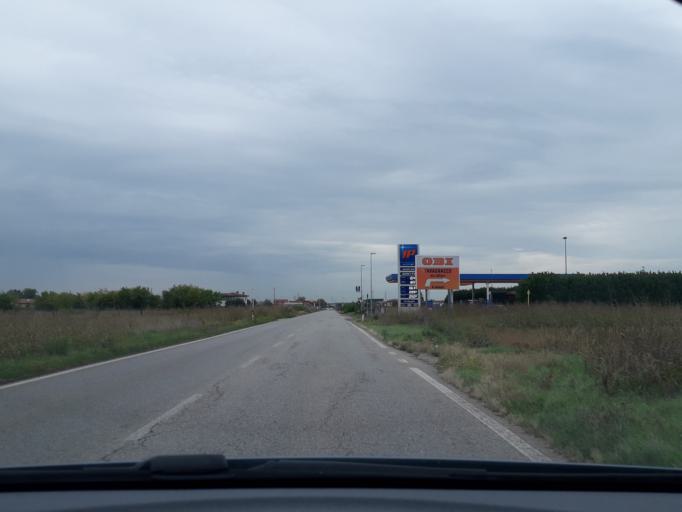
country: IT
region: Friuli Venezia Giulia
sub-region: Provincia di Udine
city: Povoletto
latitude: 46.1077
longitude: 13.2661
